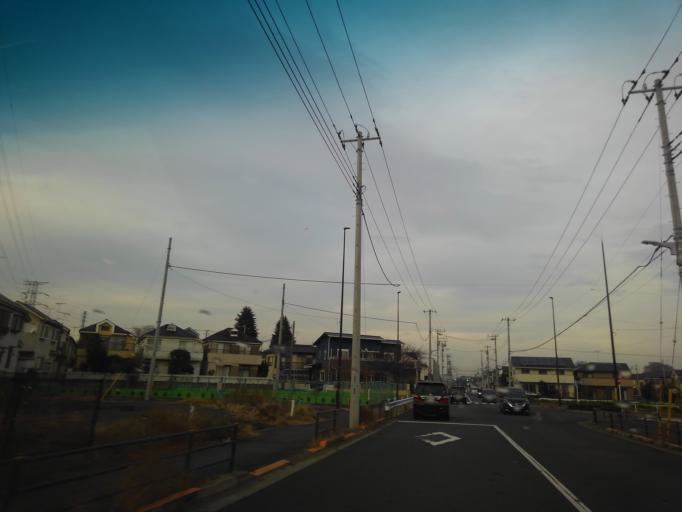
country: JP
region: Tokyo
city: Higashimurayama-shi
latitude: 35.7271
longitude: 139.4435
